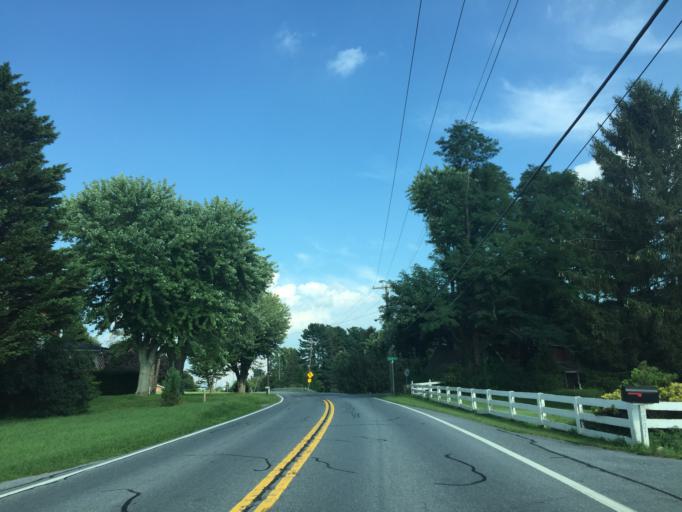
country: US
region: Maryland
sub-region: Carroll County
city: Hampstead
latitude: 39.5928
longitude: -76.7468
